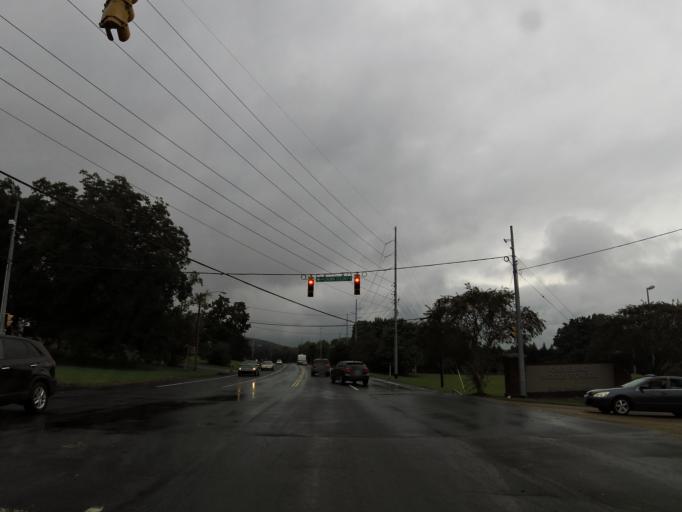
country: US
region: Tennessee
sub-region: Bradley County
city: Hopewell
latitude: 35.2043
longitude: -84.8885
